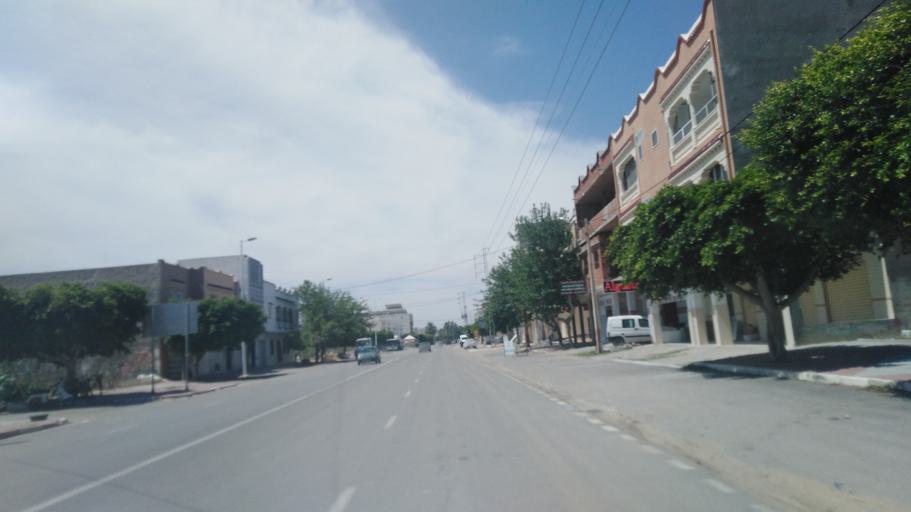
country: TN
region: Al Mahdiyah
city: Ksour Essaf
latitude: 35.4292
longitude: 11.0017
